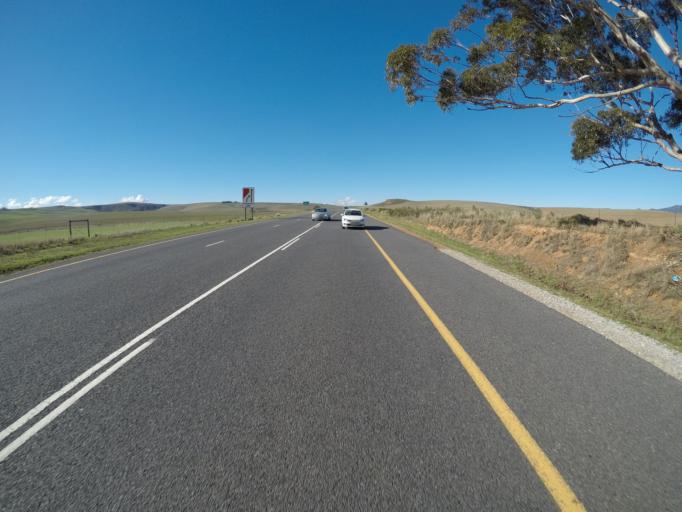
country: ZA
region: Western Cape
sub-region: Overberg District Municipality
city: Hermanus
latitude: -34.2342
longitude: 19.2313
